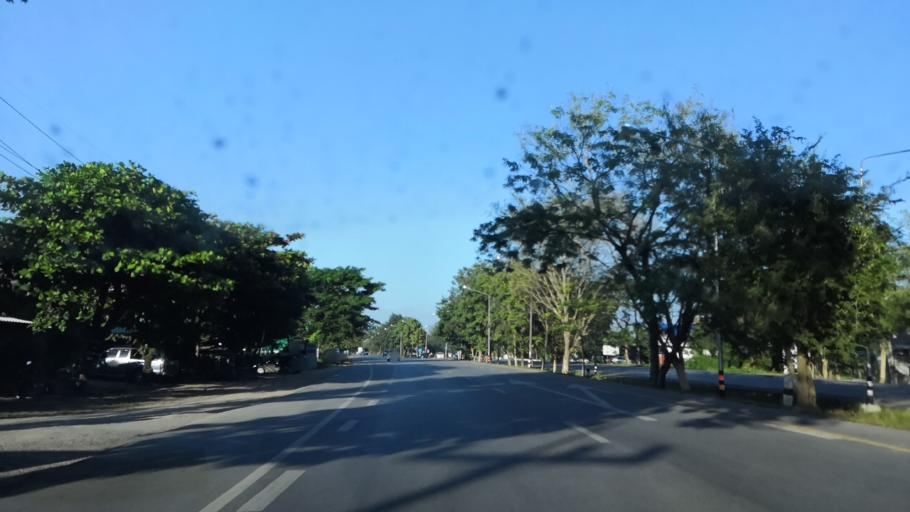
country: TH
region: Chiang Rai
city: Mae Lao
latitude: 19.7558
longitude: 99.7325
